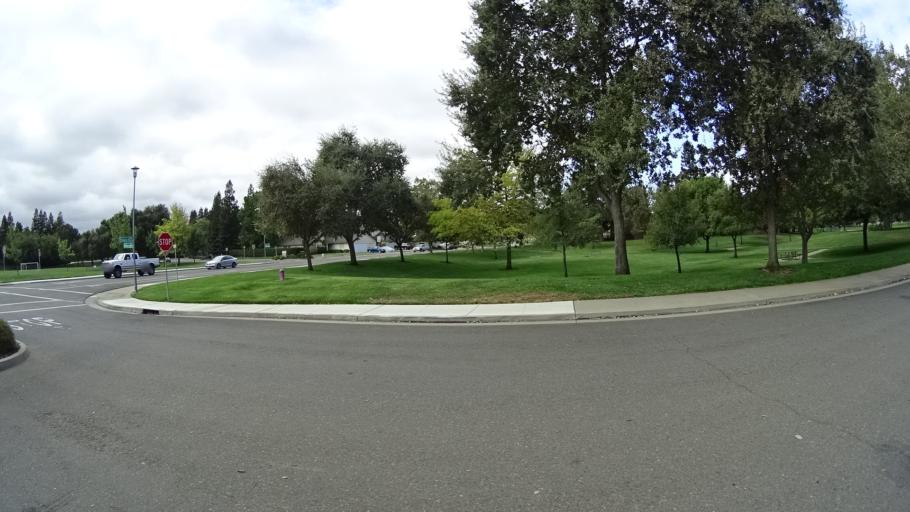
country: US
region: California
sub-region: Sacramento County
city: Laguna
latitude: 38.4192
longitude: -121.4271
